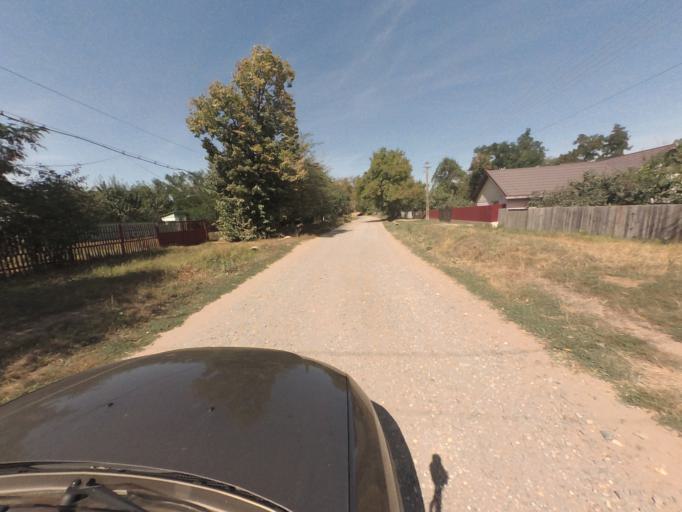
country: RO
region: Vaslui
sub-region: Comuna Deleni
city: Deleni
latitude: 46.5349
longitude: 27.7540
